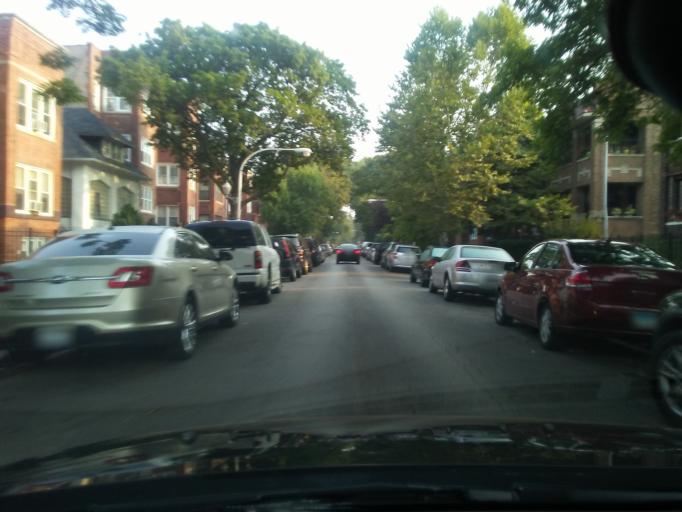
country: US
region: Illinois
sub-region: Cook County
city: Lincolnwood
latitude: 41.9705
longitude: -87.7061
